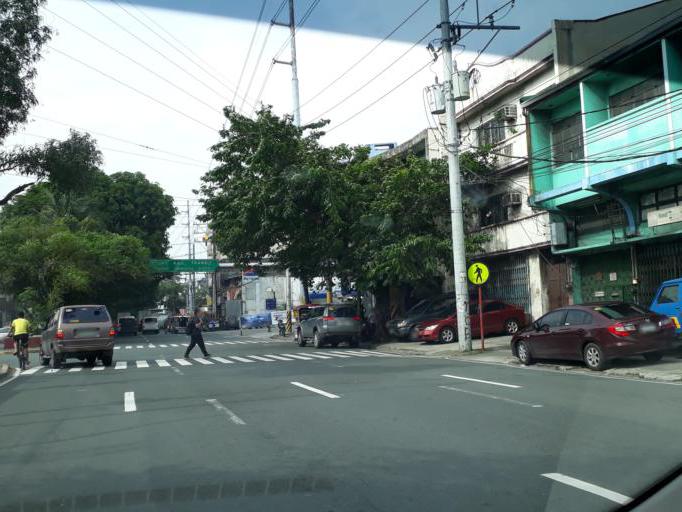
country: PH
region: Metro Manila
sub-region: City of Manila
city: Manila
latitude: 14.6301
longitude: 120.9800
